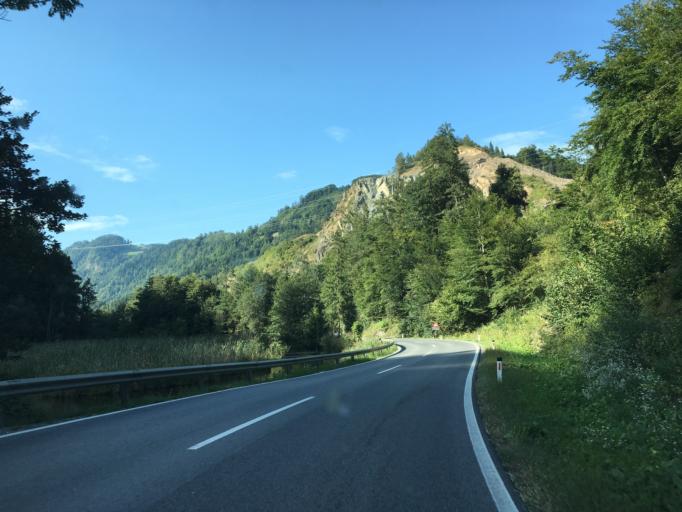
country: AT
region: Carinthia
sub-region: Politischer Bezirk Volkermarkt
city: Diex
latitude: 46.7026
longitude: 14.5683
